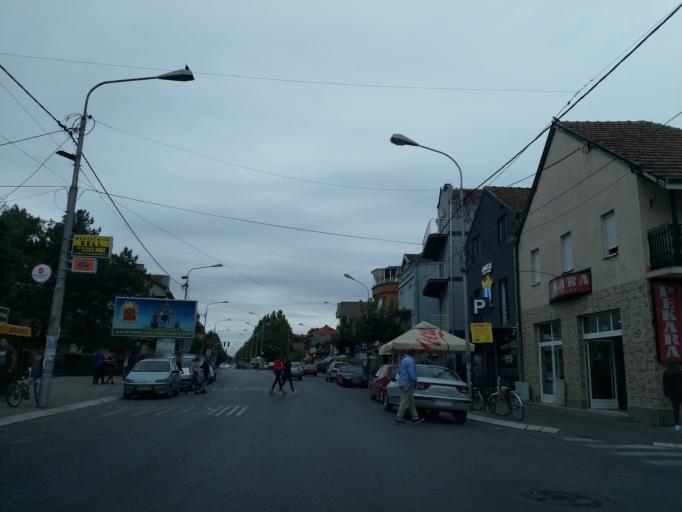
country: RS
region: Central Serbia
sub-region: Pomoravski Okrug
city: Jagodina
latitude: 43.9748
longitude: 21.2646
